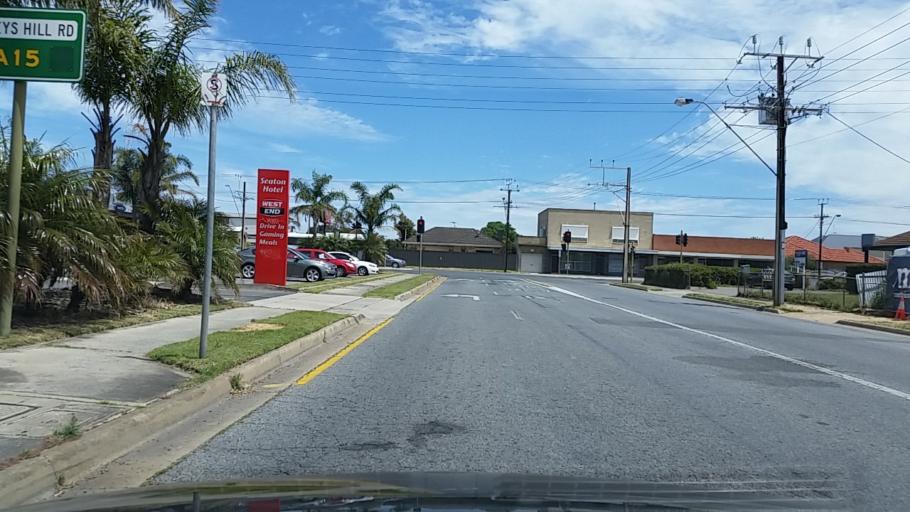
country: AU
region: South Australia
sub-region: Charles Sturt
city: Seaton
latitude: -34.8900
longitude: 138.5144
